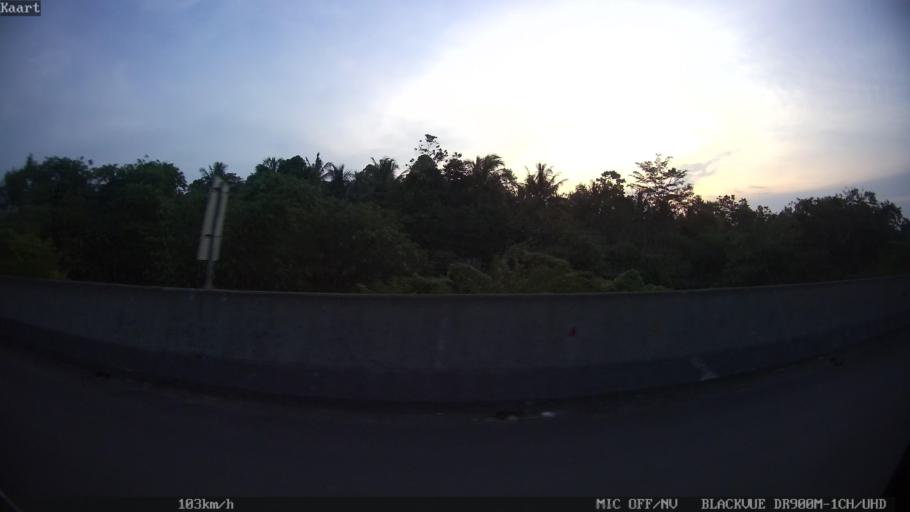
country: ID
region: Lampung
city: Penengahan
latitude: -5.7768
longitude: 105.7188
